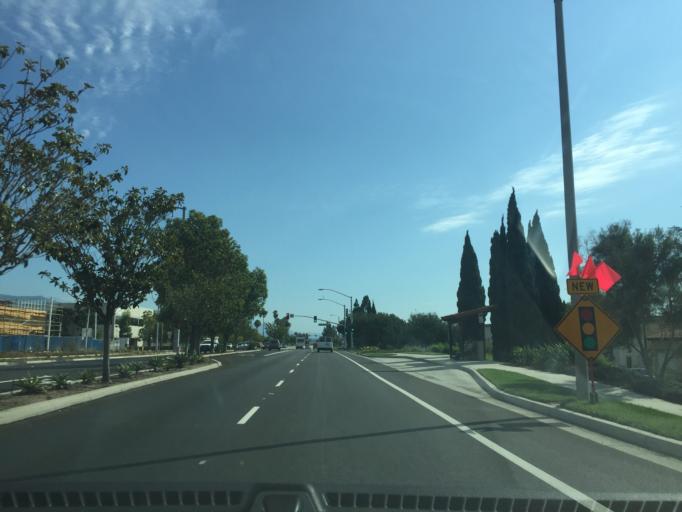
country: US
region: California
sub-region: Santa Barbara County
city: Isla Vista
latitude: 34.4301
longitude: -119.8730
